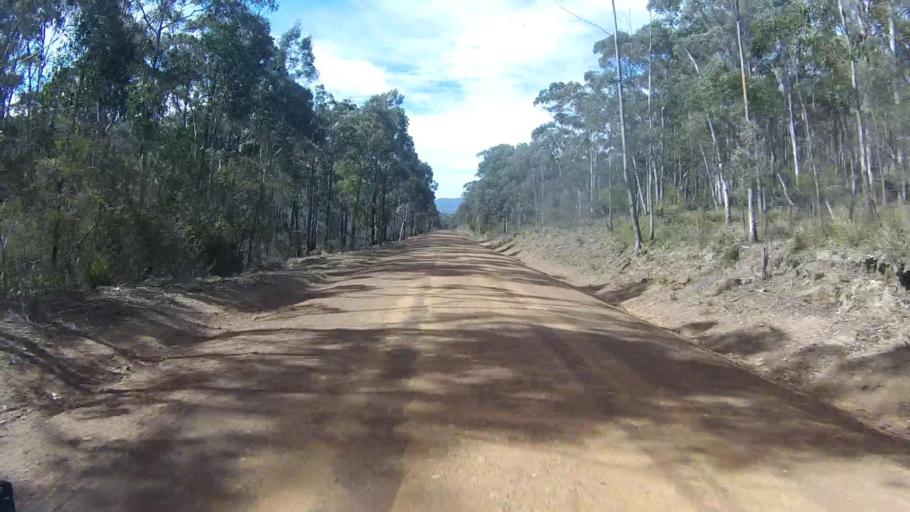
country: AU
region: Tasmania
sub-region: Sorell
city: Sorell
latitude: -42.6169
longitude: 147.9003
